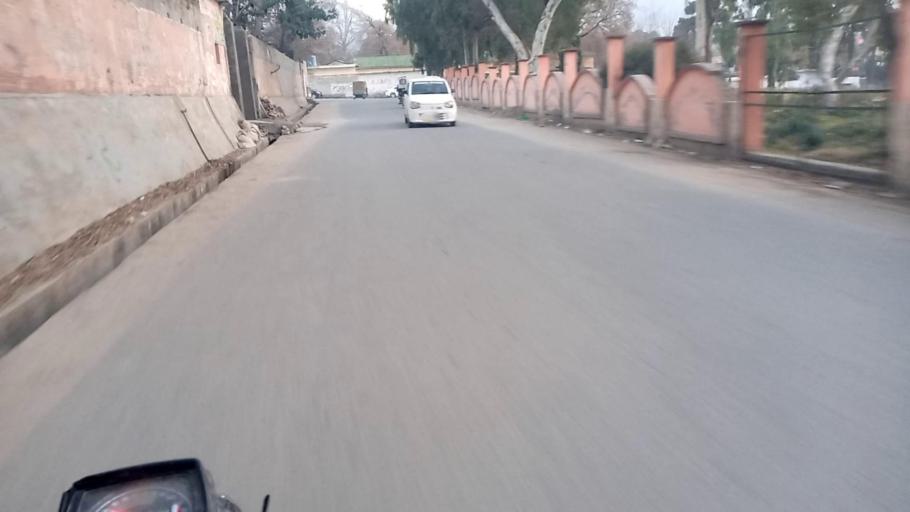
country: PK
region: Khyber Pakhtunkhwa
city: Saidu Sharif
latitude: 34.7611
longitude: 72.3599
